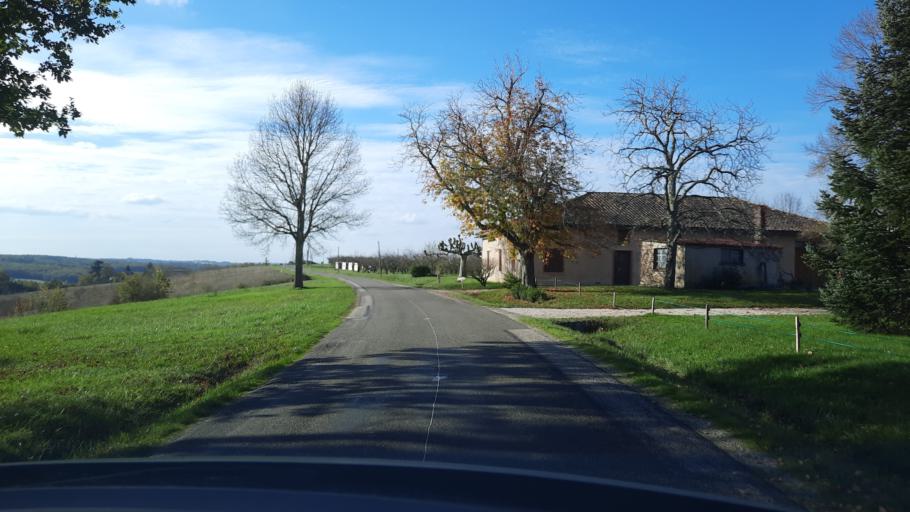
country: FR
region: Midi-Pyrenees
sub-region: Departement du Tarn-et-Garonne
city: Molieres
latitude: 44.1413
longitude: 1.3234
